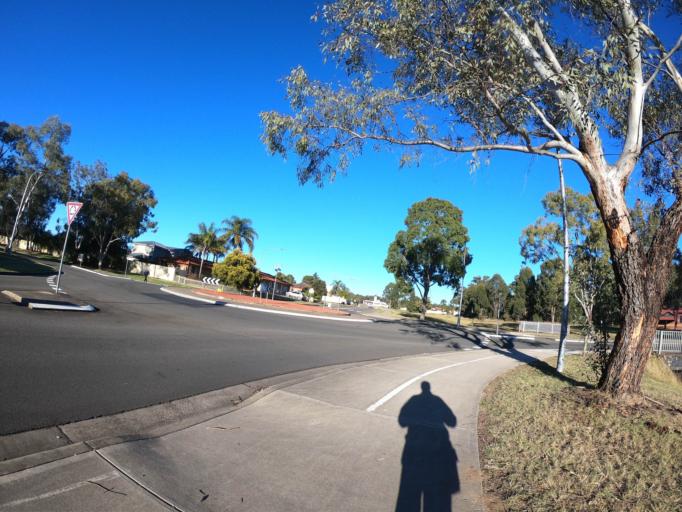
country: AU
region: New South Wales
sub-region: Hawkesbury
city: South Windsor
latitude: -33.6375
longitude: 150.8055
